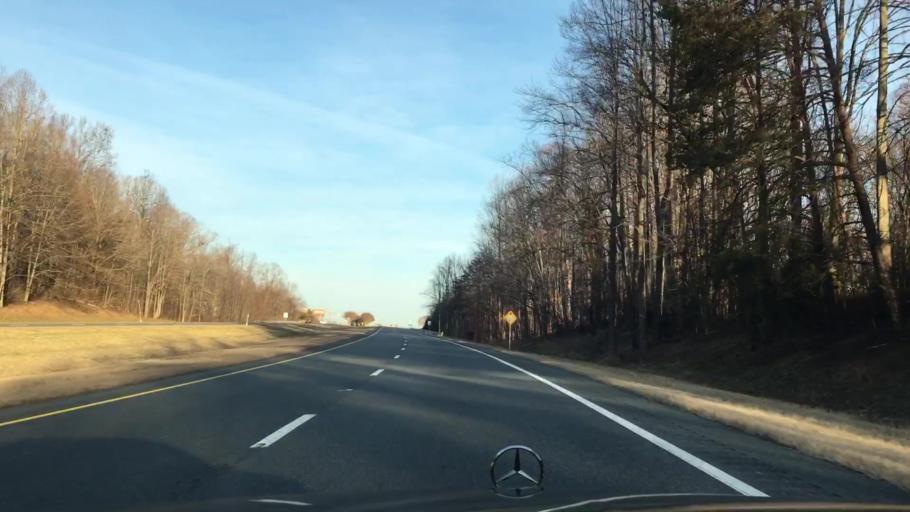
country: US
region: North Carolina
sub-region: Guilford County
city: Greensboro
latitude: 36.0244
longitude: -79.7658
